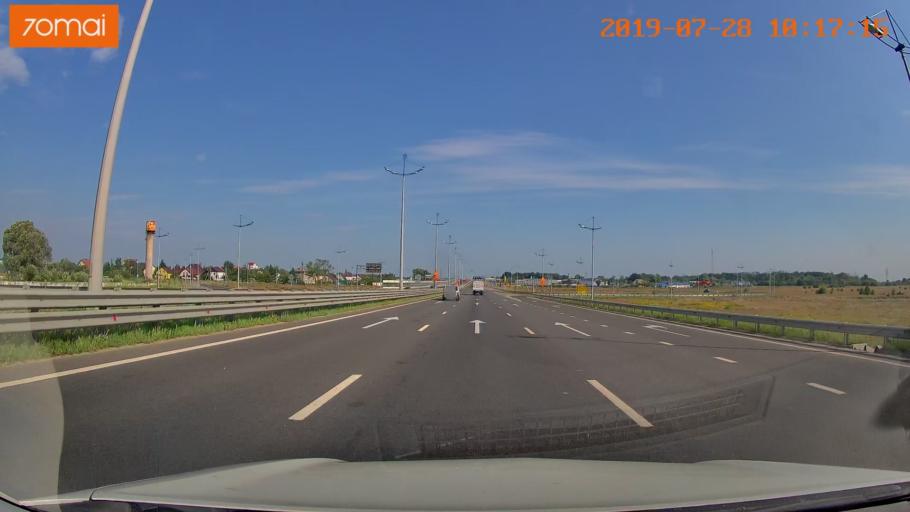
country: RU
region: Kaliningrad
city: Maloye Isakovo
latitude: 54.7376
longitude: 20.5954
